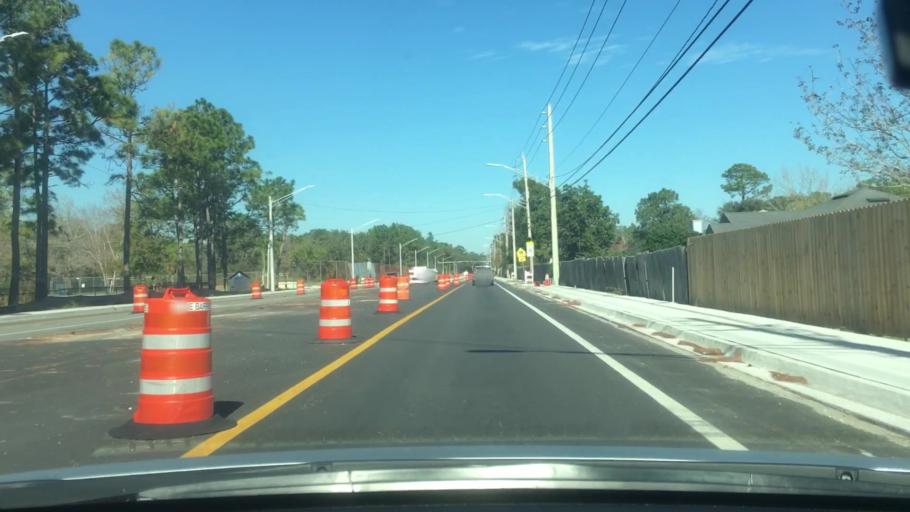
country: US
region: Florida
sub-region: Duval County
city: Atlantic Beach
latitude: 30.3212
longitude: -81.4726
